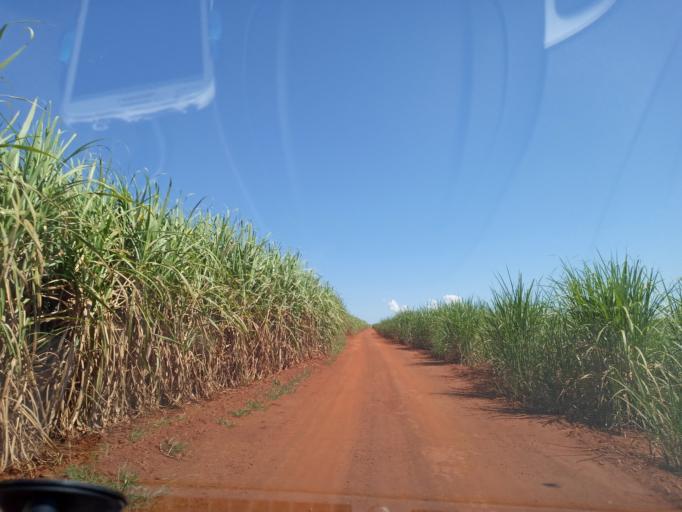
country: BR
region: Goias
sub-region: Itumbiara
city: Itumbiara
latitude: -18.4361
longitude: -49.1497
